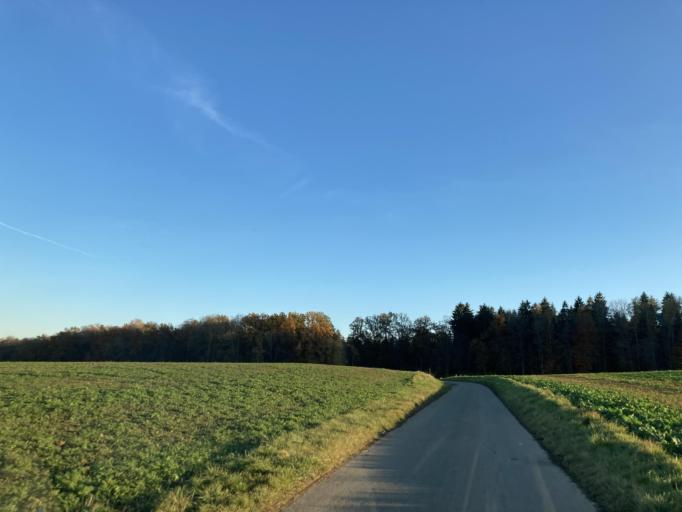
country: DE
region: Baden-Wuerttemberg
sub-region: Tuebingen Region
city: Hirrlingen
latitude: 48.4416
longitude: 8.8885
